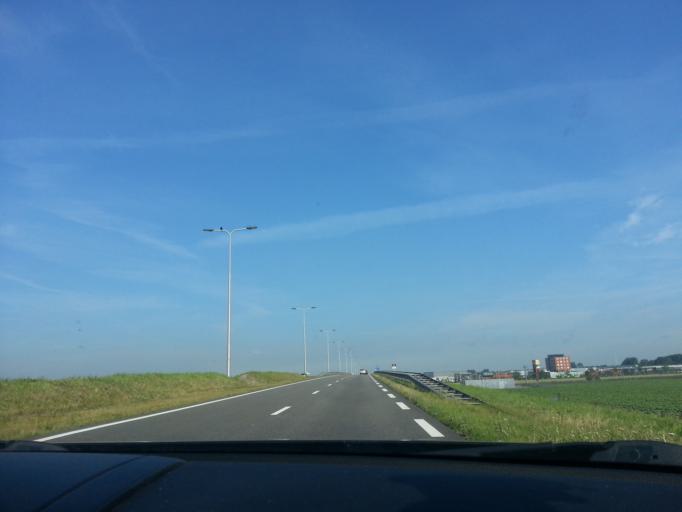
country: NL
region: South Holland
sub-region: Gemeente Kaag en Braassem
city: Oude Wetering
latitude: 52.2469
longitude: 4.6405
